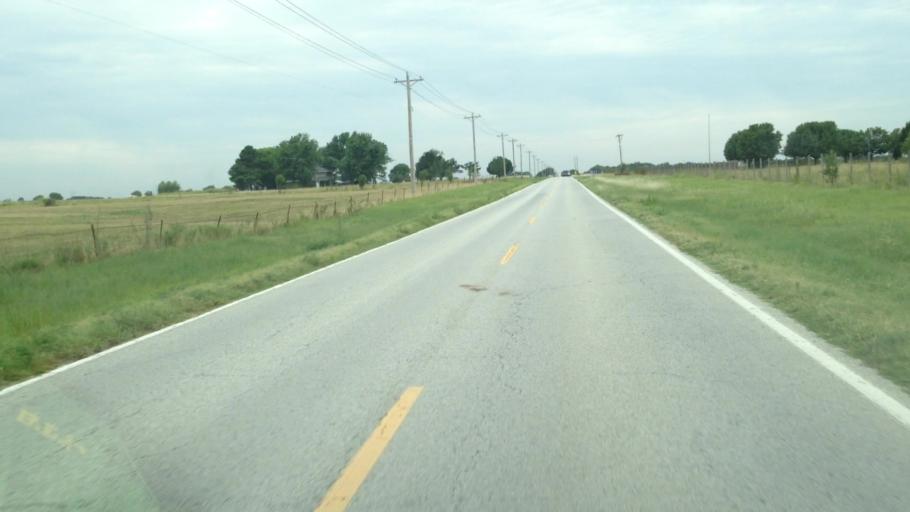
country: US
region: Oklahoma
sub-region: Delaware County
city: Cleora
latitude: 36.6126
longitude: -94.9729
